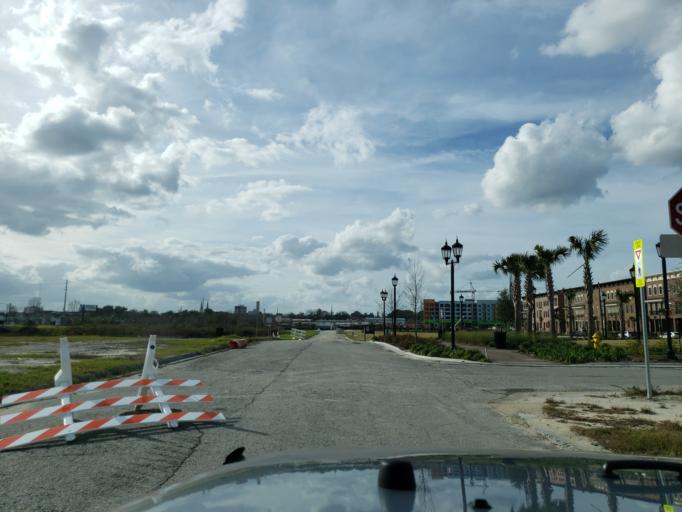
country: US
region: Georgia
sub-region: Chatham County
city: Savannah
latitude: 32.0758
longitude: -81.0754
